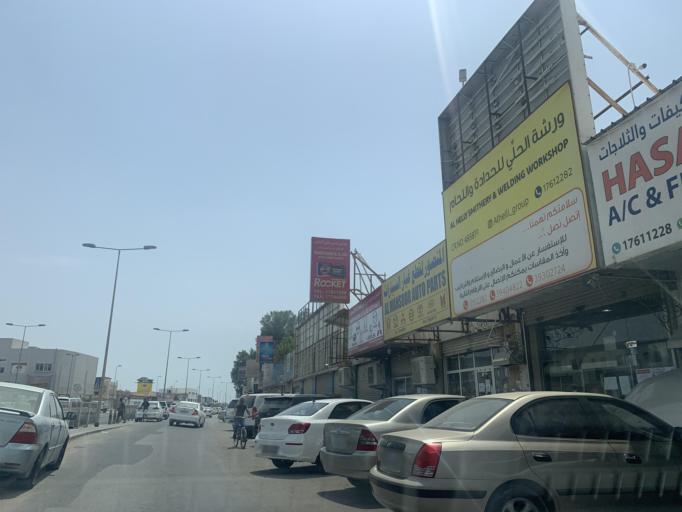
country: BH
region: Central Governorate
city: Madinat Hamad
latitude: 26.1431
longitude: 50.4918
